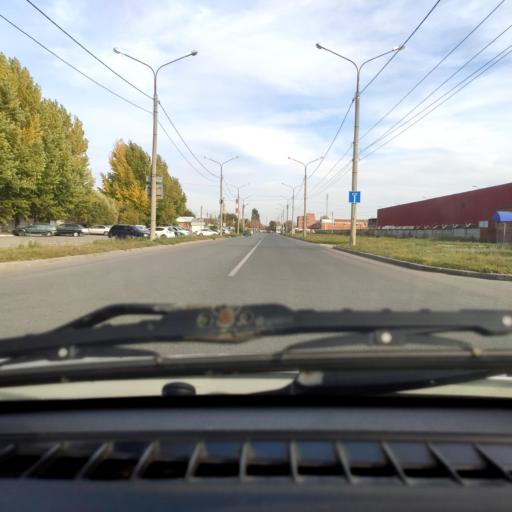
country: RU
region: Samara
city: Tol'yatti
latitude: 53.5420
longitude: 49.4191
